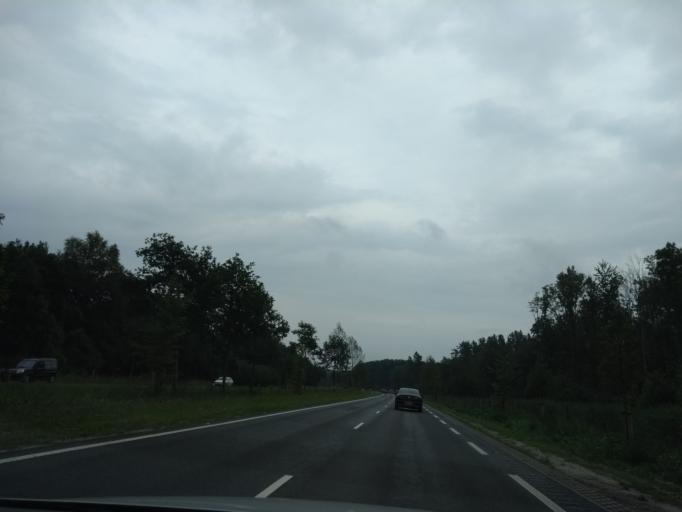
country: NL
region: North Holland
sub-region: Gemeente Huizen
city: Huizen
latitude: 52.3467
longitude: 5.2613
